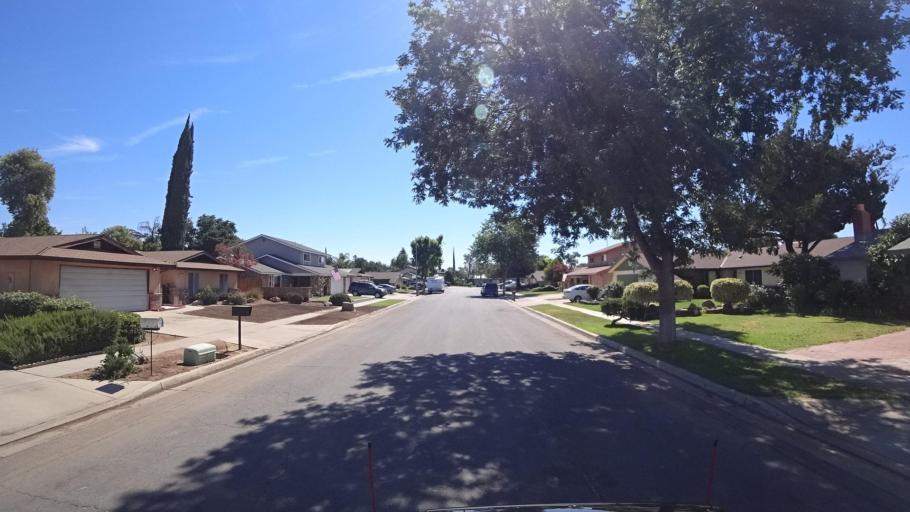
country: US
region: California
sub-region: Fresno County
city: Sunnyside
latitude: 36.7388
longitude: -119.7160
